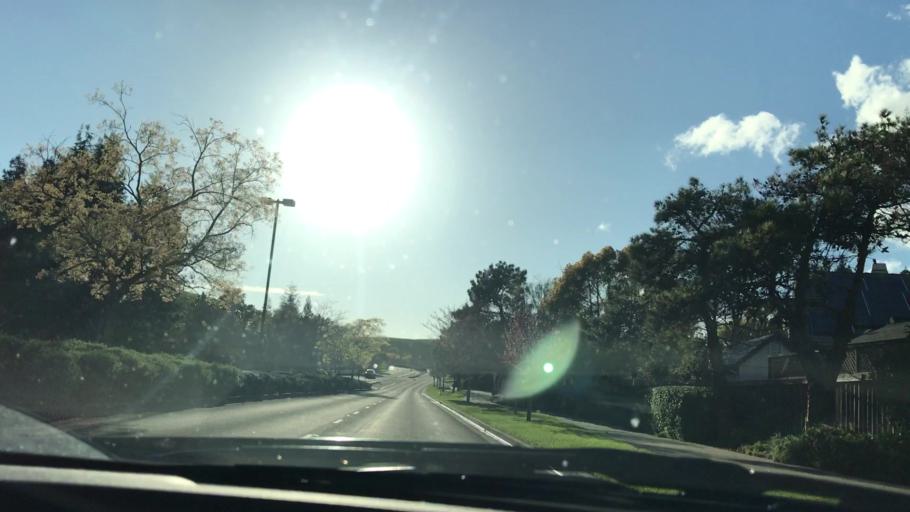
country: US
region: California
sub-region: Solano County
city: Fairfield
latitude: 38.2894
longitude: -122.0452
